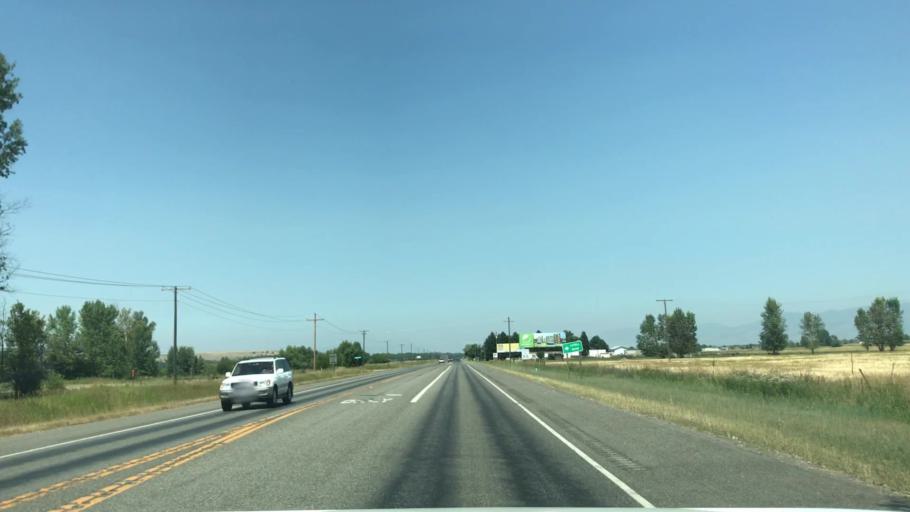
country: US
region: Montana
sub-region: Gallatin County
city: Four Corners
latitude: 45.6221
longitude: -111.1969
